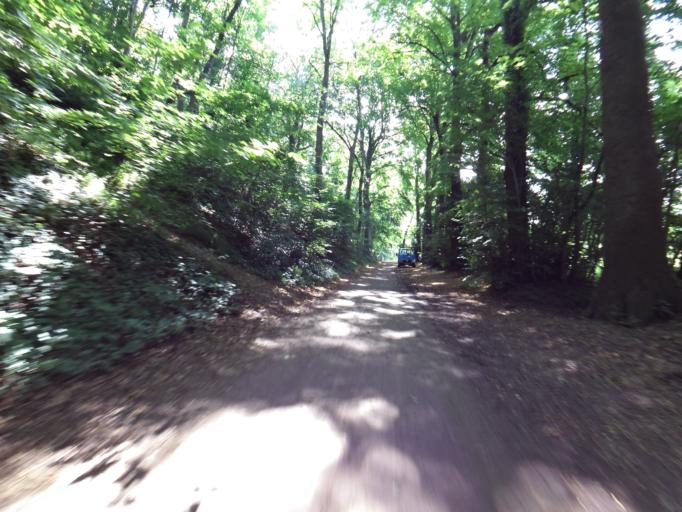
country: NL
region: Limburg
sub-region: Valkenburg aan de Geul
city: Valkenburg
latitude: 50.8590
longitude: 5.8481
